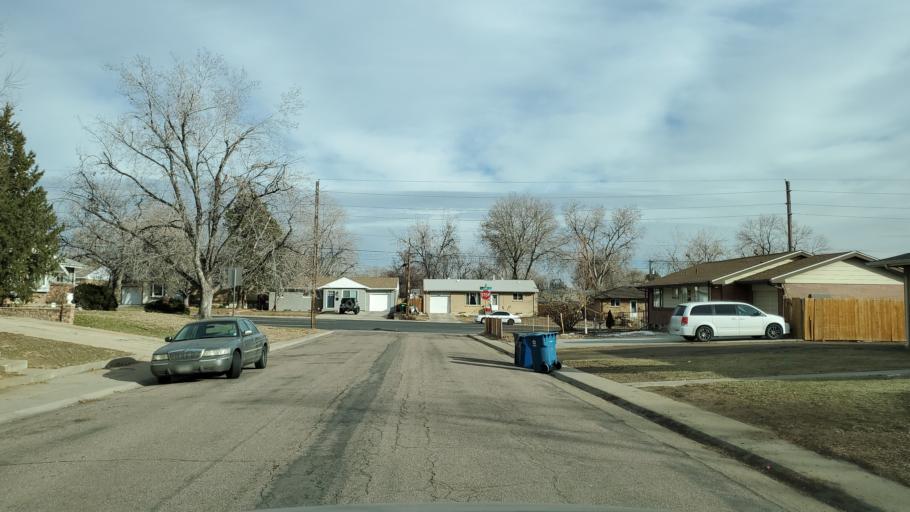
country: US
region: Colorado
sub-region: Adams County
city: Sherrelwood
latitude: 39.8355
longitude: -105.0163
